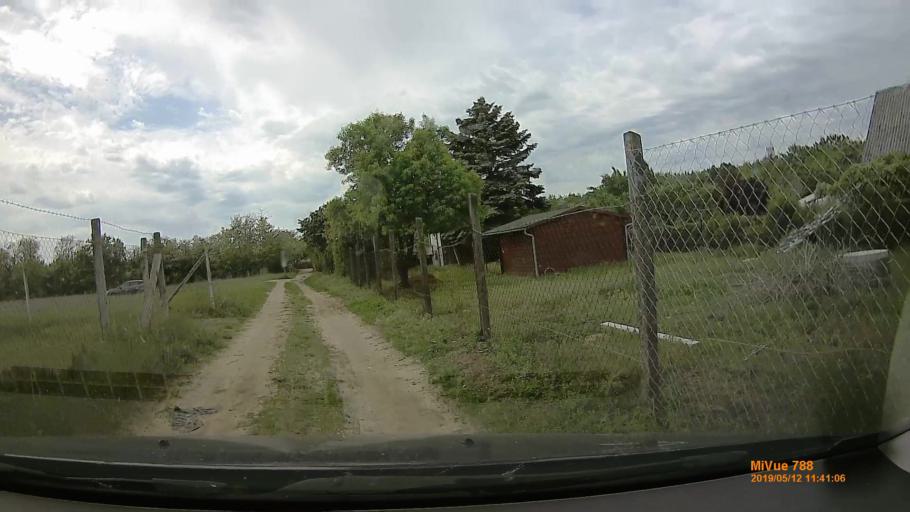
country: HU
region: Budapest
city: Budapest XVII. keruelet
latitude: 47.4629
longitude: 19.2568
